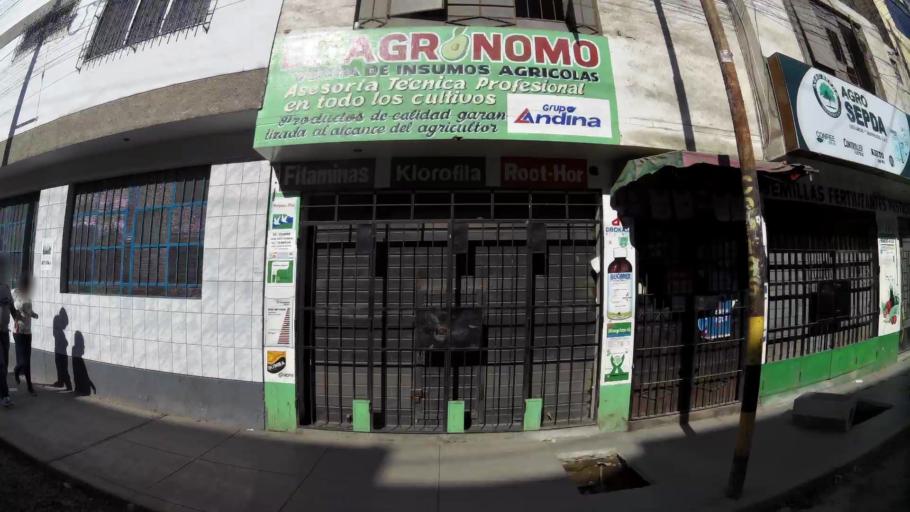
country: PE
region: Ica
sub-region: Provincia de Chincha
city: Chincha Alta
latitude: -13.4185
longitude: -76.1360
